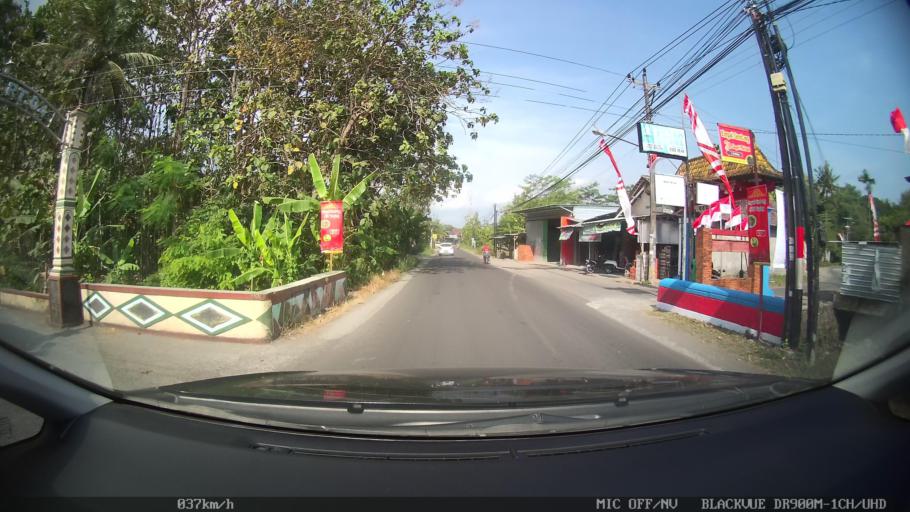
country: ID
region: Daerah Istimewa Yogyakarta
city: Kasihan
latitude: -7.8418
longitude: 110.3296
